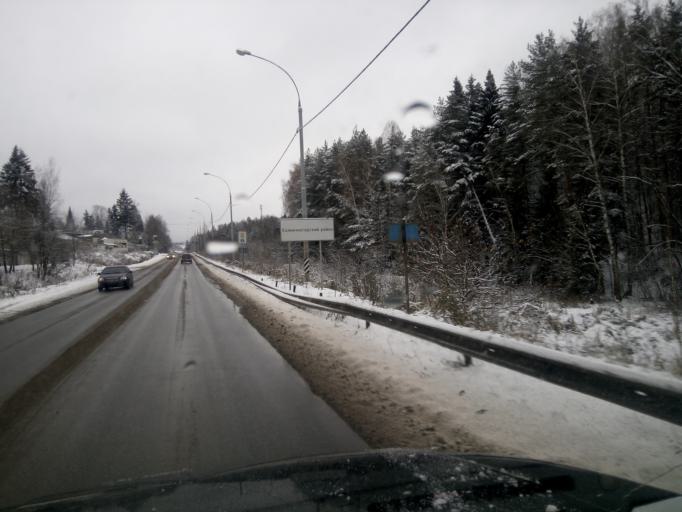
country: RU
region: Moskovskaya
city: Skhodnya
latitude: 55.9637
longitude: 37.3096
